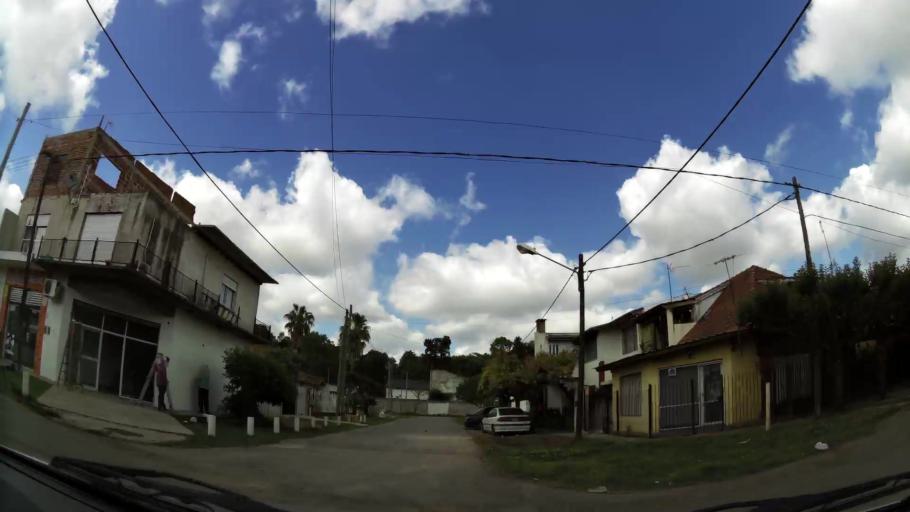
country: AR
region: Buenos Aires
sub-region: Partido de Quilmes
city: Quilmes
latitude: -34.8290
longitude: -58.1846
